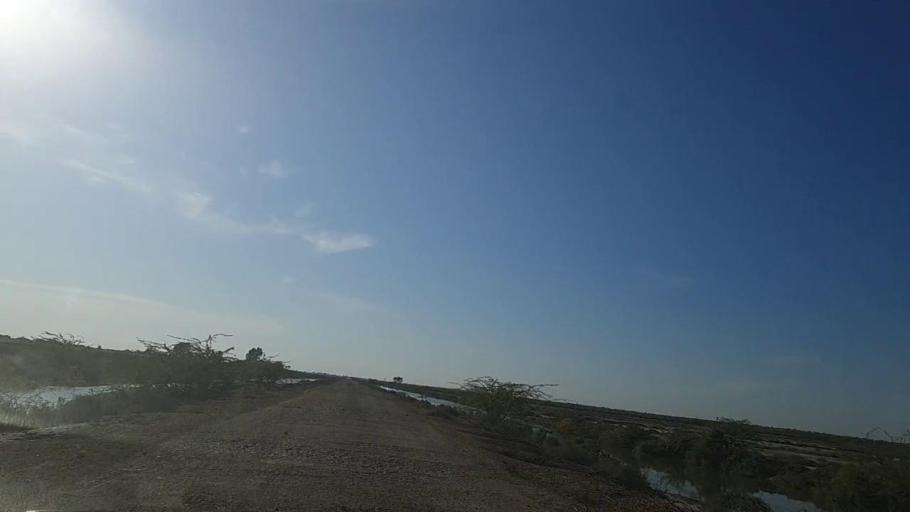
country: PK
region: Sindh
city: Pithoro
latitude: 25.5093
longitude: 69.4347
